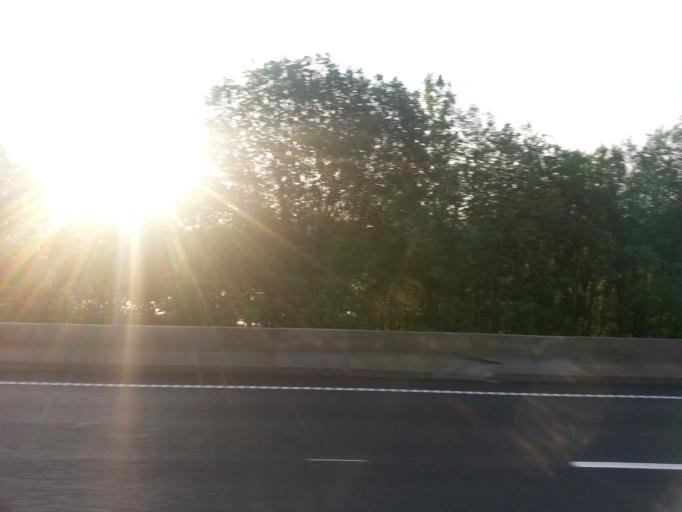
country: NO
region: Sor-Trondelag
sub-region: Malvik
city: Hommelvik
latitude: 63.4144
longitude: 10.7688
